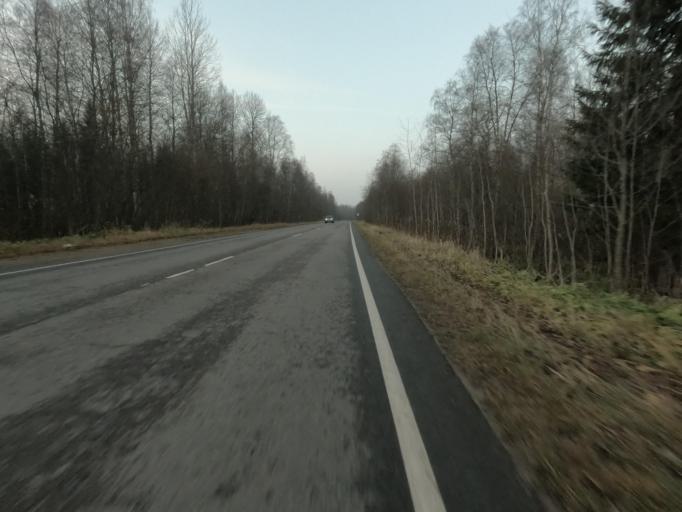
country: RU
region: Leningrad
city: Kirovsk
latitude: 59.8545
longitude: 30.9917
